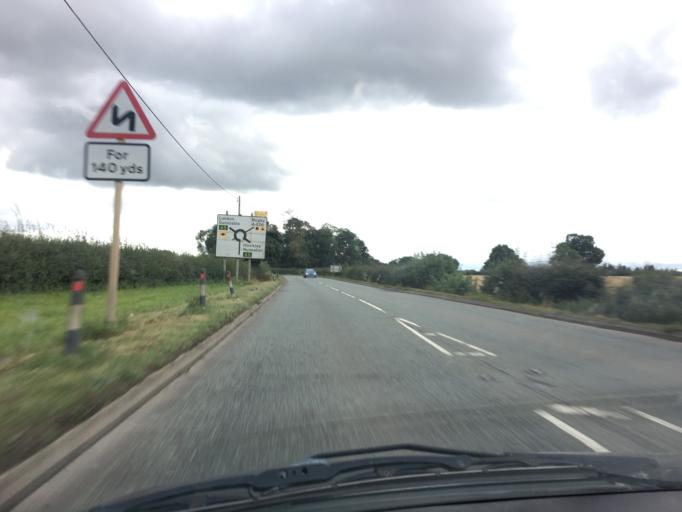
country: GB
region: England
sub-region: Leicestershire
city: Lutterworth
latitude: 52.4253
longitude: -1.2236
